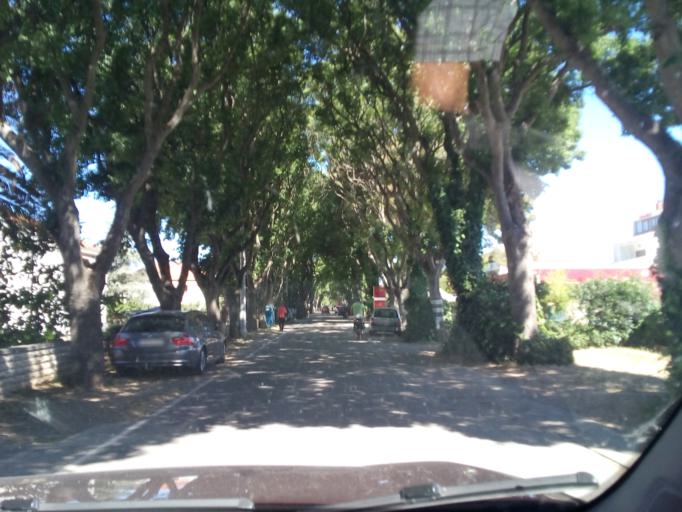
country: HR
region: Zadarska
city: Zadar
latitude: 44.1326
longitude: 15.2196
